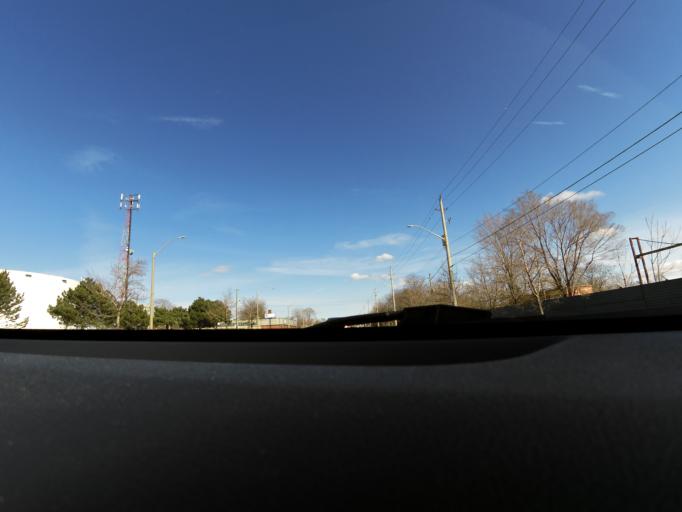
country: CA
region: Ontario
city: Hamilton
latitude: 43.2688
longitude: -79.8457
